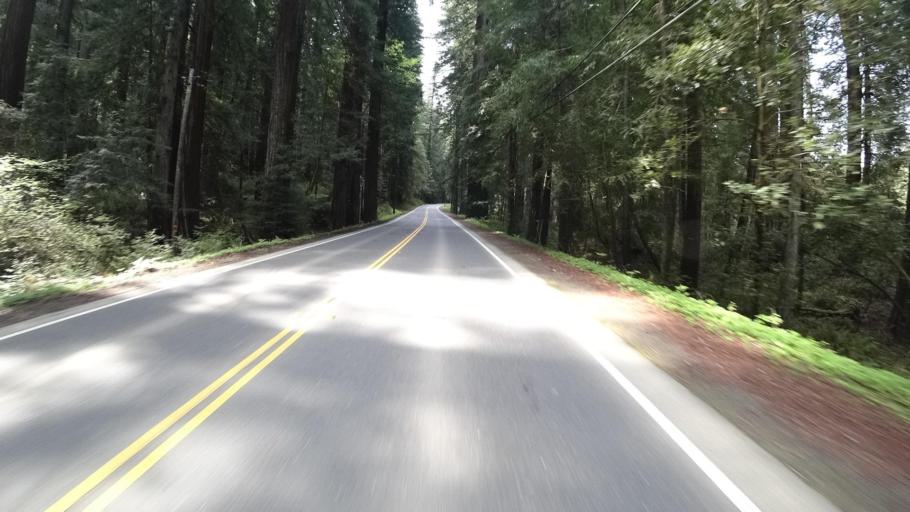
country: US
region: California
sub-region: Humboldt County
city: Redway
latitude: 40.1348
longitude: -123.8165
